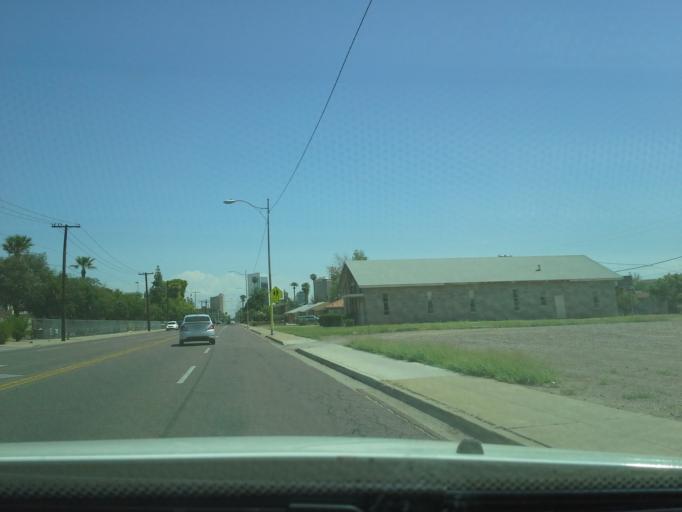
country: US
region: Arizona
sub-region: Maricopa County
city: Phoenix
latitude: 33.4877
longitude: -112.0911
